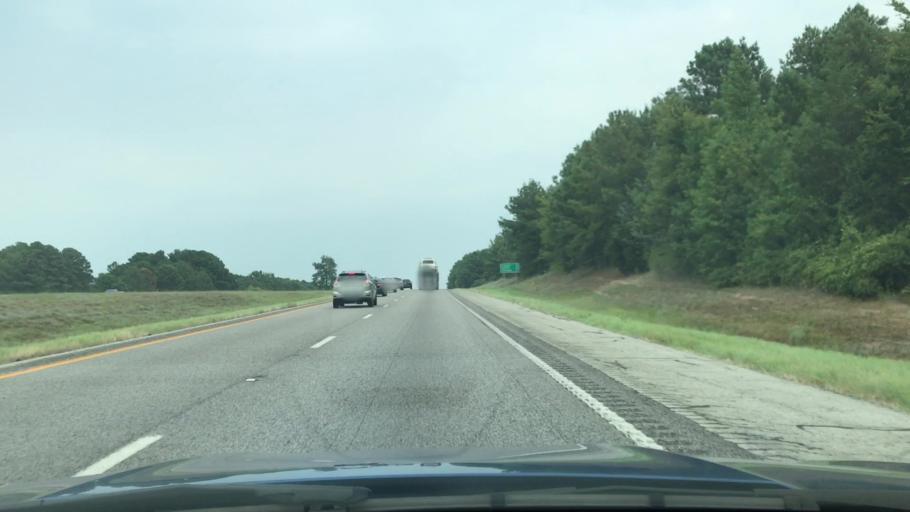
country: US
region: Texas
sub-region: Smith County
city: Lindale
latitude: 32.4684
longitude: -95.3557
